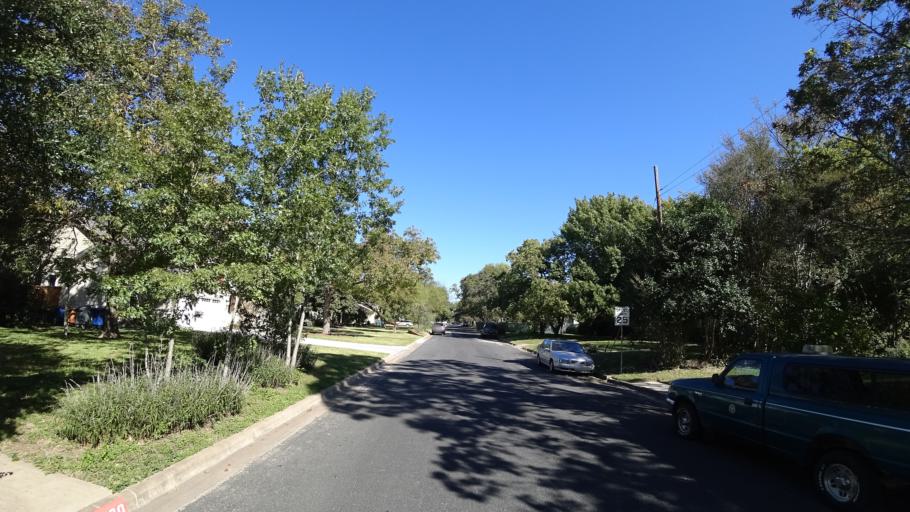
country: US
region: Texas
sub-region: Travis County
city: Austin
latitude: 30.3337
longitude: -97.7445
